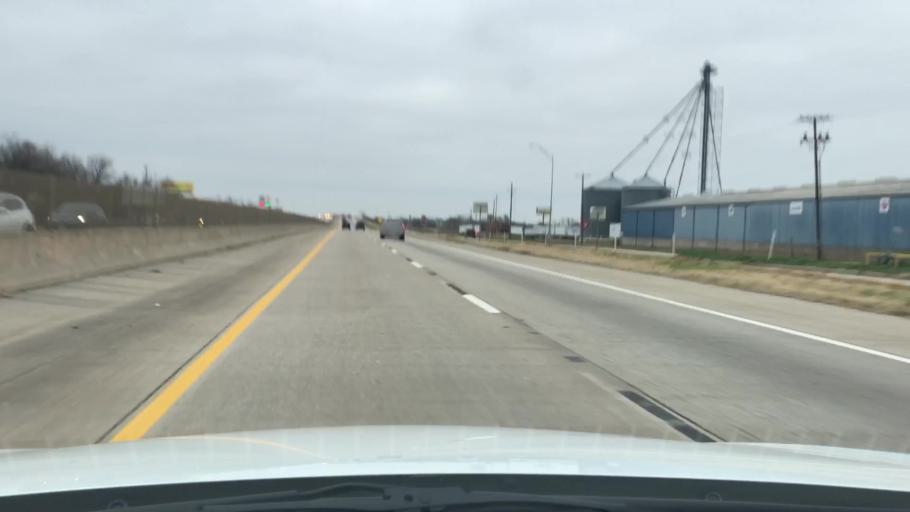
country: US
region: Texas
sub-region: Denton County
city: Sanger
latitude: 33.4827
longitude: -97.1621
